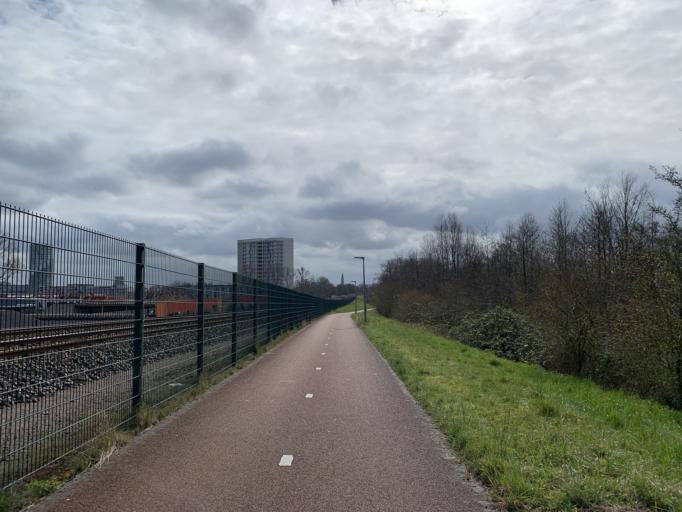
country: NL
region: Groningen
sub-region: Gemeente Groningen
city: Korrewegwijk
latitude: 53.2414
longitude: 6.5574
